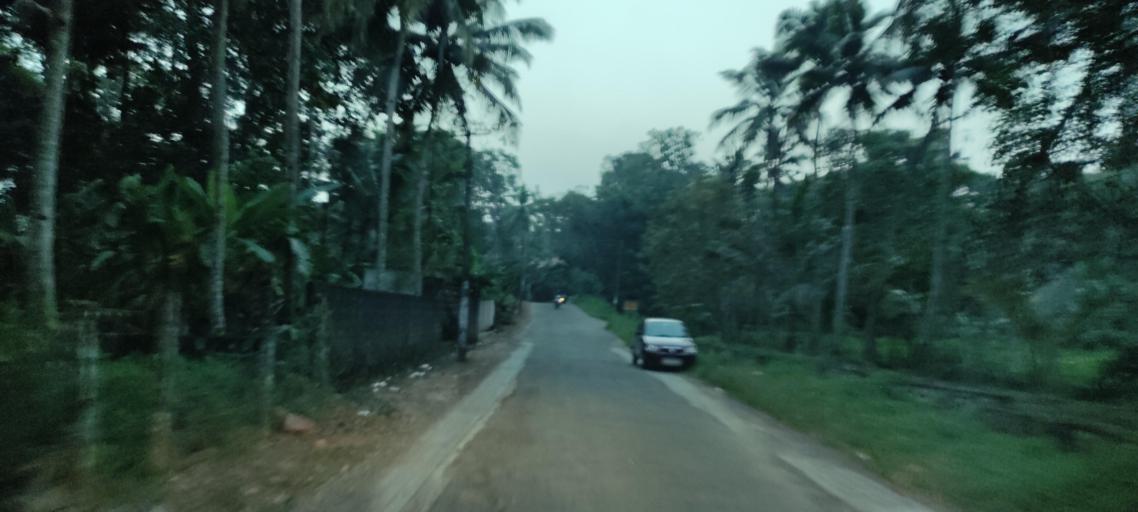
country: IN
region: Kerala
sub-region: Pattanamtitta
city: Adur
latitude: 9.1577
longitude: 76.7375
